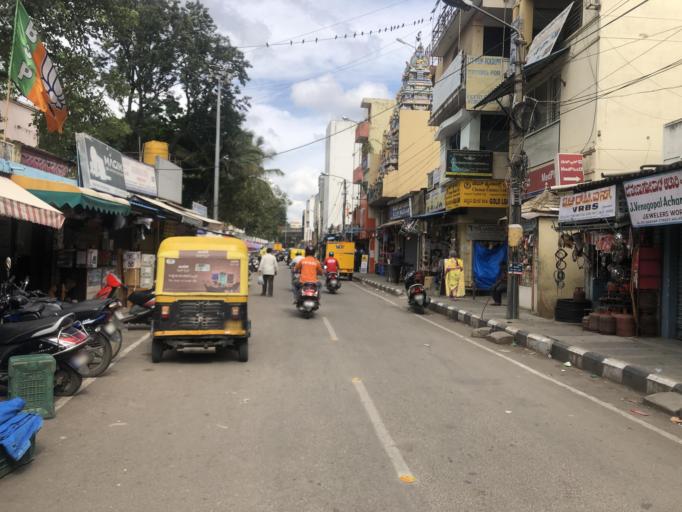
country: IN
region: Karnataka
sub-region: Bangalore Urban
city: Bangalore
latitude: 12.9754
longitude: 77.6231
